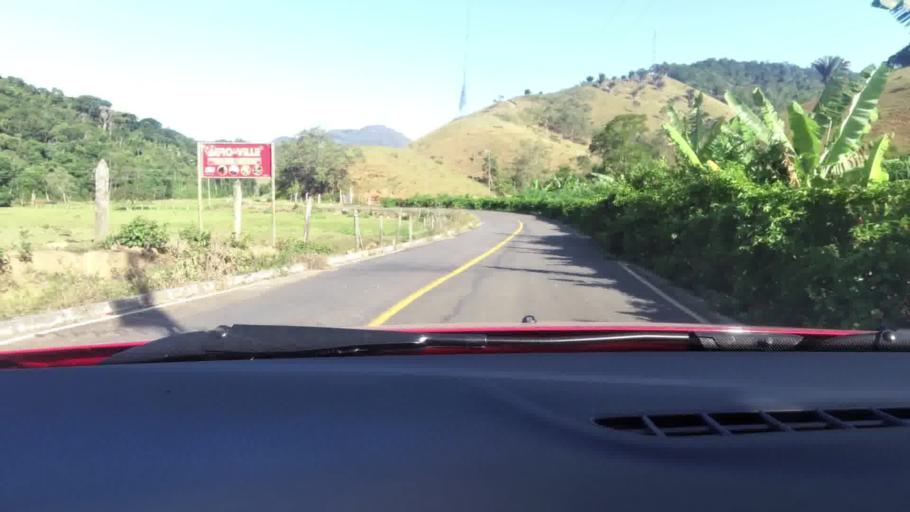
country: BR
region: Espirito Santo
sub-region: Guarapari
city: Guarapari
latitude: -20.5617
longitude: -40.5515
